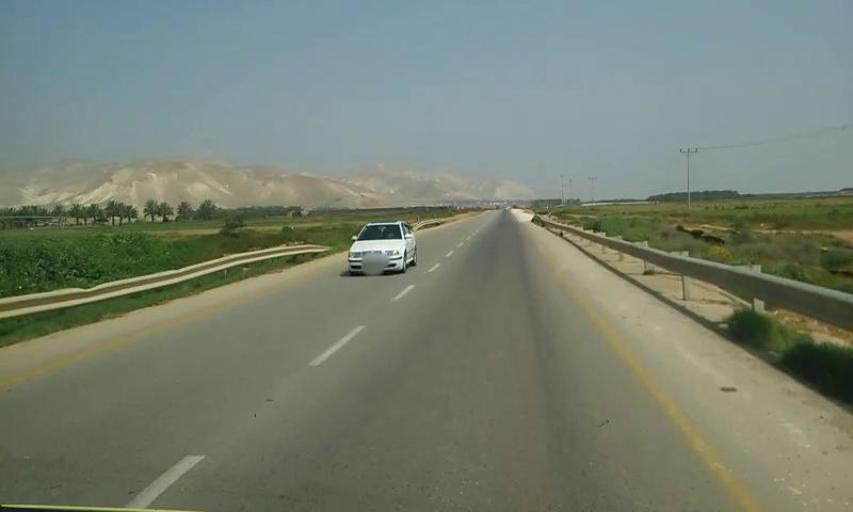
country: PS
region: West Bank
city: Al Fasayil
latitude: 32.0345
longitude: 35.4549
